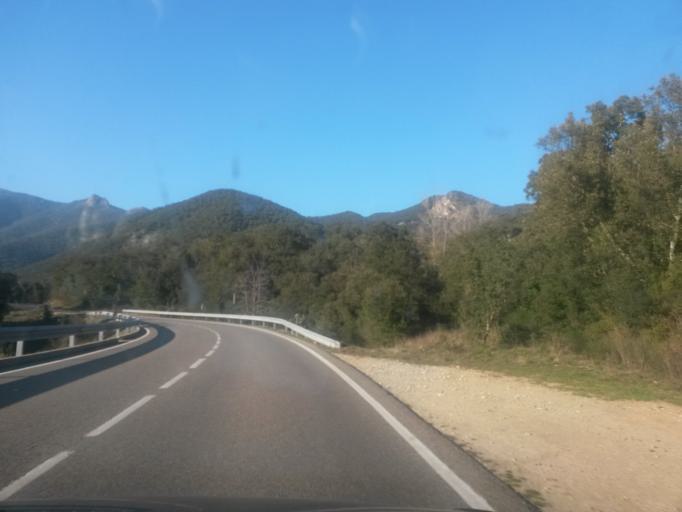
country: ES
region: Catalonia
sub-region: Provincia de Girona
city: Macanet de Cabrenys
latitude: 42.3831
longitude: 2.7876
